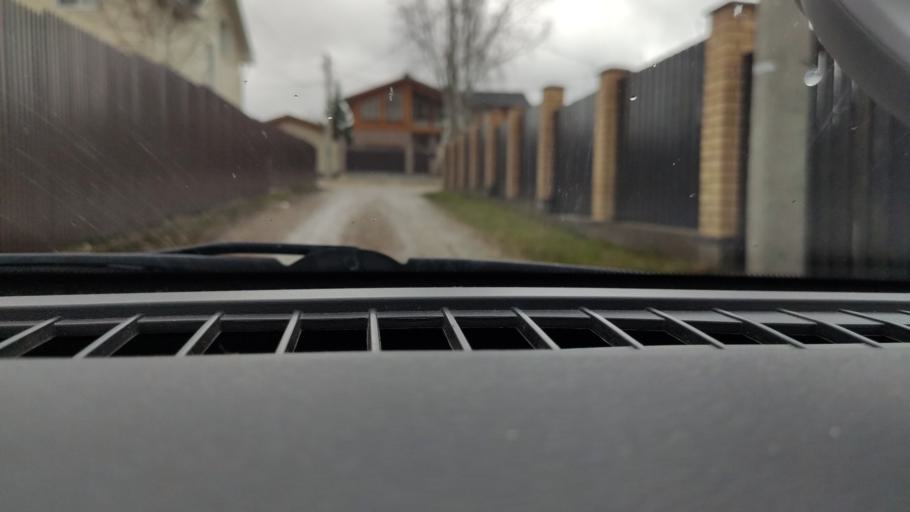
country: RU
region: Perm
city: Froly
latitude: 57.9477
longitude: 56.3071
